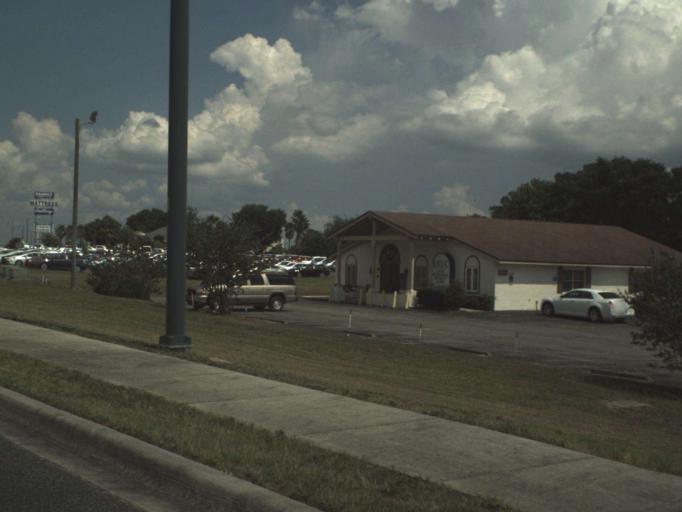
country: US
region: Florida
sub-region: Lake County
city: Silver Lake
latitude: 28.8322
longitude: -81.8178
